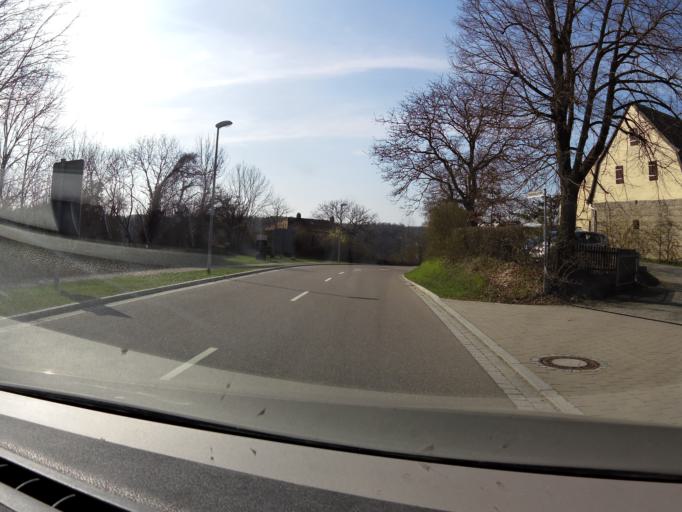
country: DE
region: Bavaria
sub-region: Regierungsbezirk Mittelfranken
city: Rothenburg ob der Tauber
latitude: 49.3826
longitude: 10.1748
